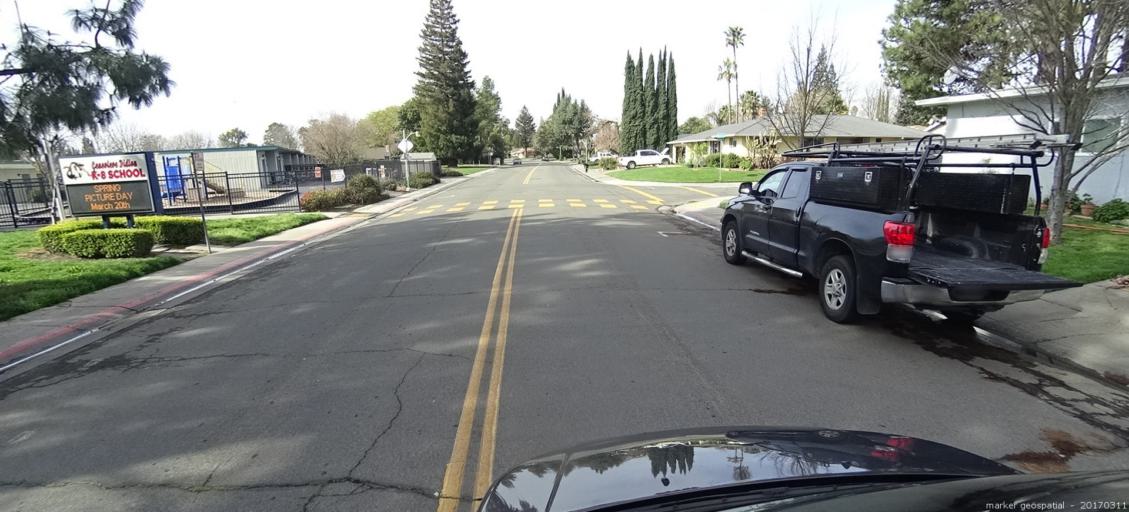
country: US
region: California
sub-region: Yolo County
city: West Sacramento
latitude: 38.5094
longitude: -121.5502
